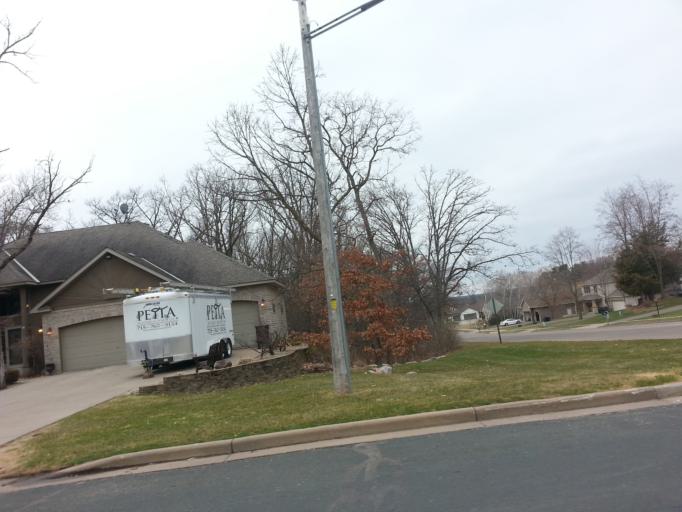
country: US
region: Wisconsin
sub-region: Saint Croix County
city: North Hudson
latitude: 45.0054
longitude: -92.7471
